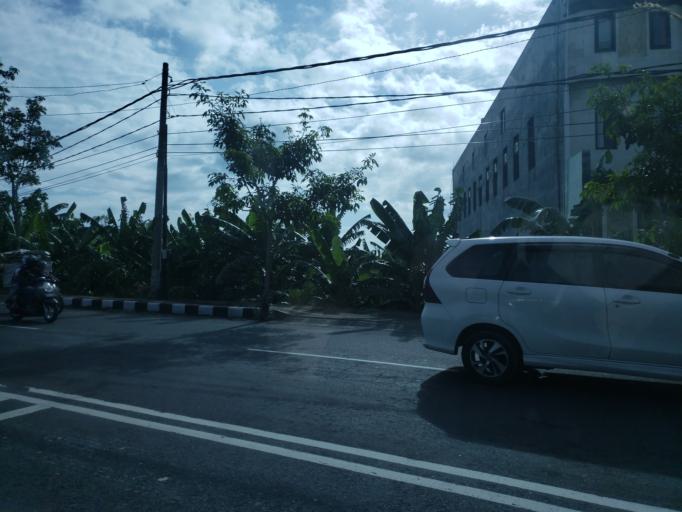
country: ID
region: Bali
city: Denpasar
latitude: -8.6727
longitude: 115.1906
